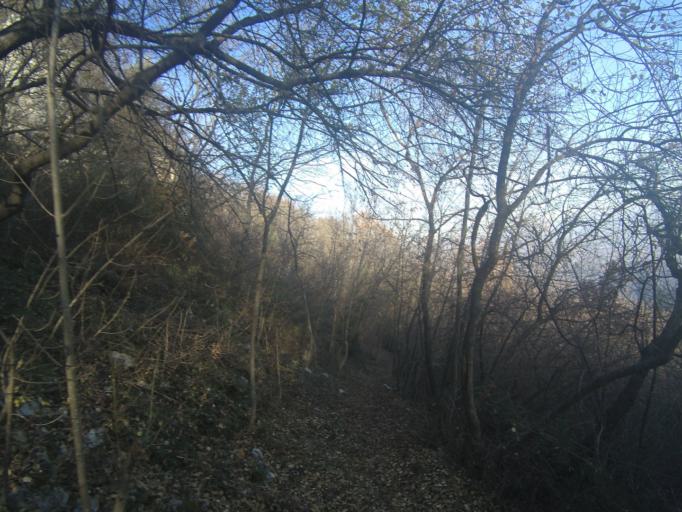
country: IT
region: Veneto
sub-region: Provincia di Vicenza
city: Lumignano
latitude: 45.4479
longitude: 11.5768
